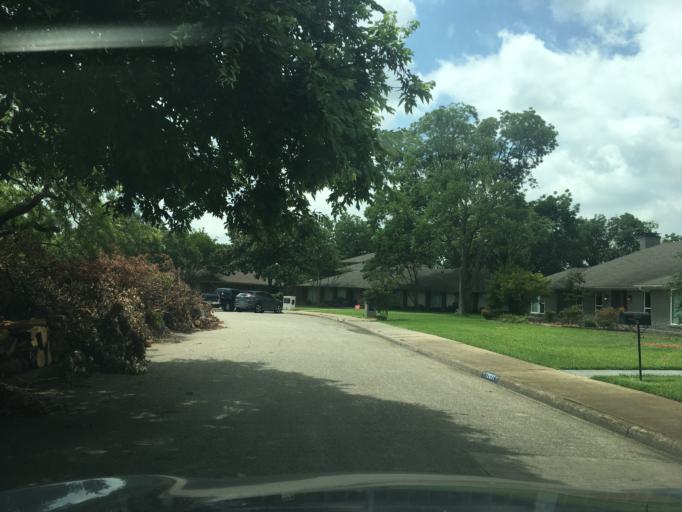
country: US
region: Texas
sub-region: Dallas County
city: Addison
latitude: 32.9137
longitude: -96.8223
